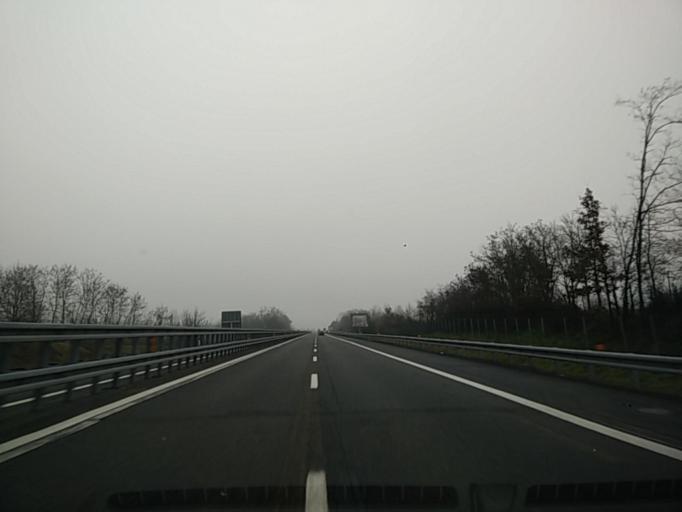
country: IT
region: Piedmont
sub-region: Provincia di Asti
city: Revigliasco d'Asti
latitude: 44.9036
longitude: 8.1528
